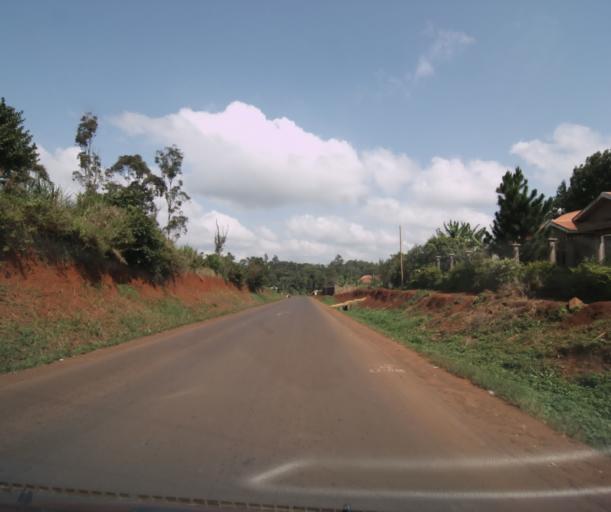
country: CM
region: West
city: Bansoa
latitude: 5.4909
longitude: 10.1895
